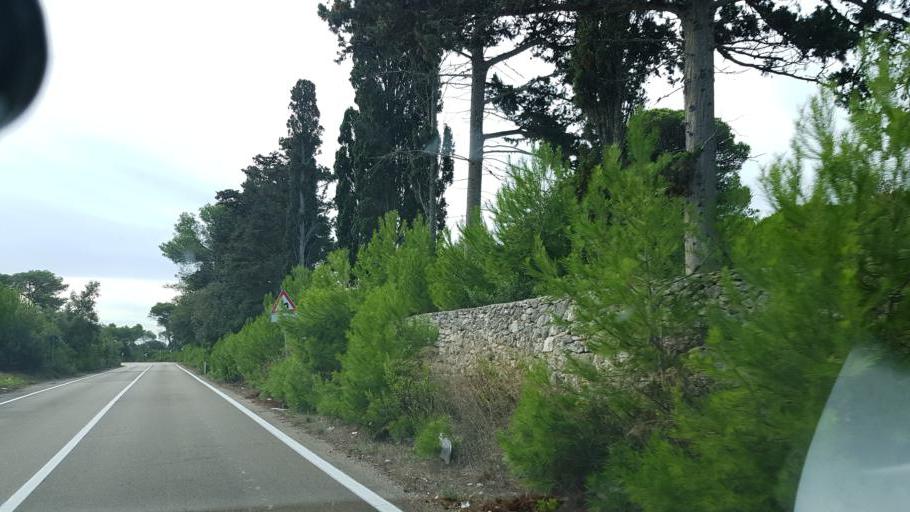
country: IT
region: Apulia
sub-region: Provincia di Lecce
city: Struda
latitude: 40.3853
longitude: 18.2975
